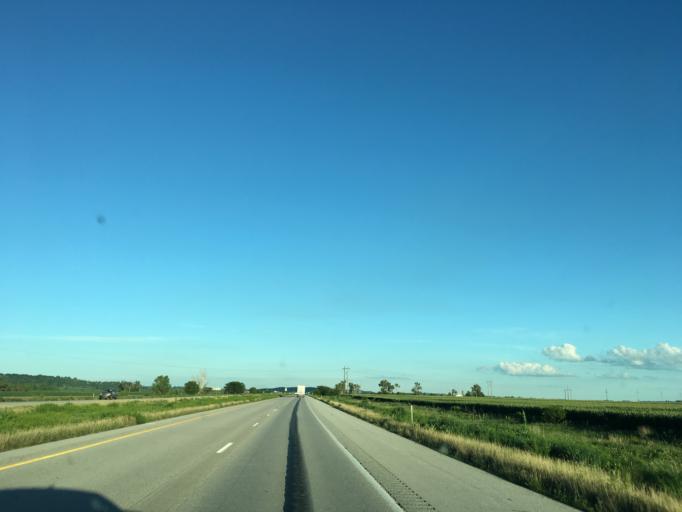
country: US
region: Iowa
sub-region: Fremont County
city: Hamburg
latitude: 40.6257
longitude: -95.7105
